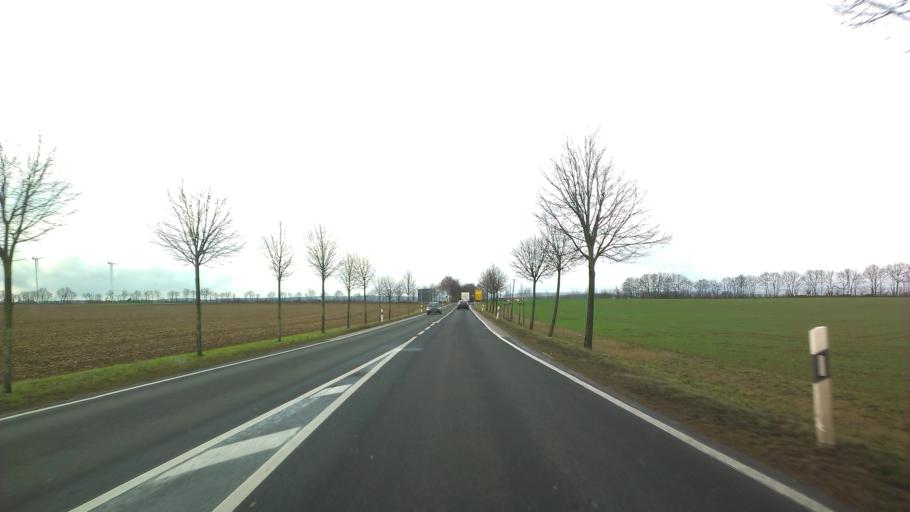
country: DE
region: Rheinland-Pfalz
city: Erbes-Budesheim
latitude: 49.7521
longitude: 8.0557
